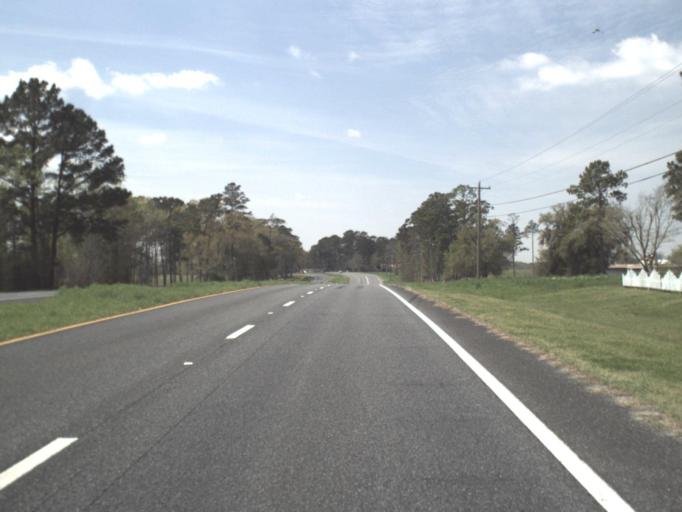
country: US
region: Florida
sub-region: Gadsden County
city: Havana
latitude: 30.6687
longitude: -84.4027
